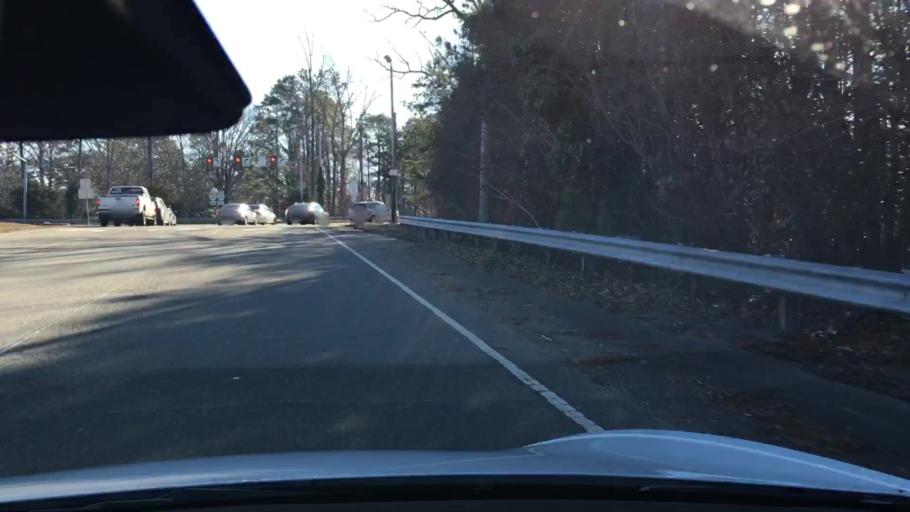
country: US
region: Virginia
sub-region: Chesterfield County
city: Bon Air
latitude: 37.5437
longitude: -77.5551
